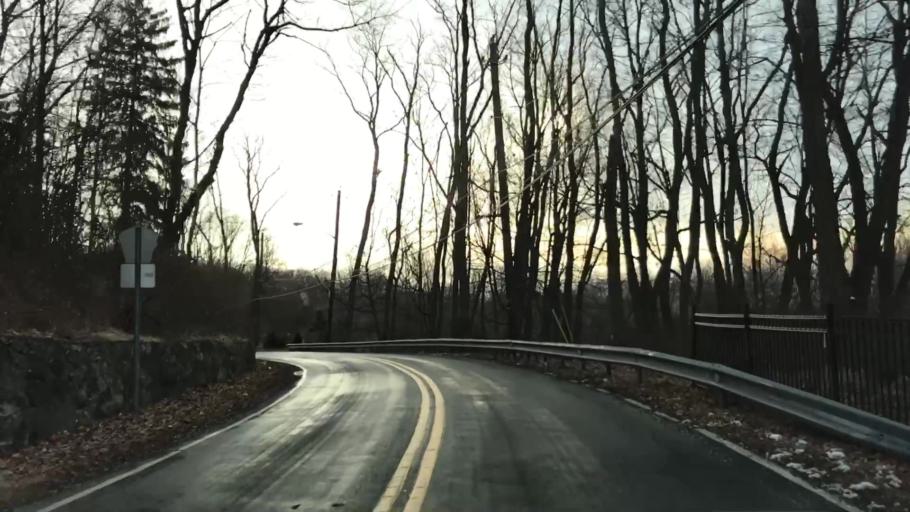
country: US
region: New York
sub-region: Rockland County
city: Stony Point
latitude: 41.2363
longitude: -74.0064
